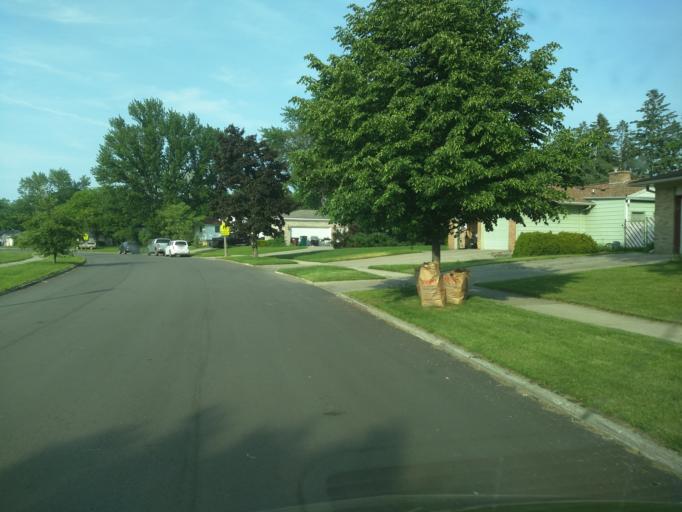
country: US
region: Michigan
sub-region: Ingham County
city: Edgemont Park
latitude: 42.7098
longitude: -84.5912
